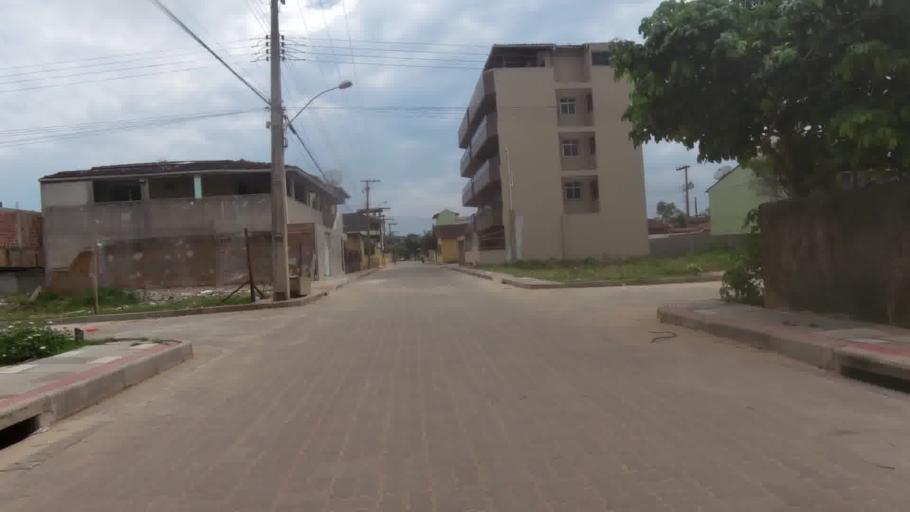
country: BR
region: Espirito Santo
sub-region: Piuma
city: Piuma
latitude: -20.8460
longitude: -40.7448
